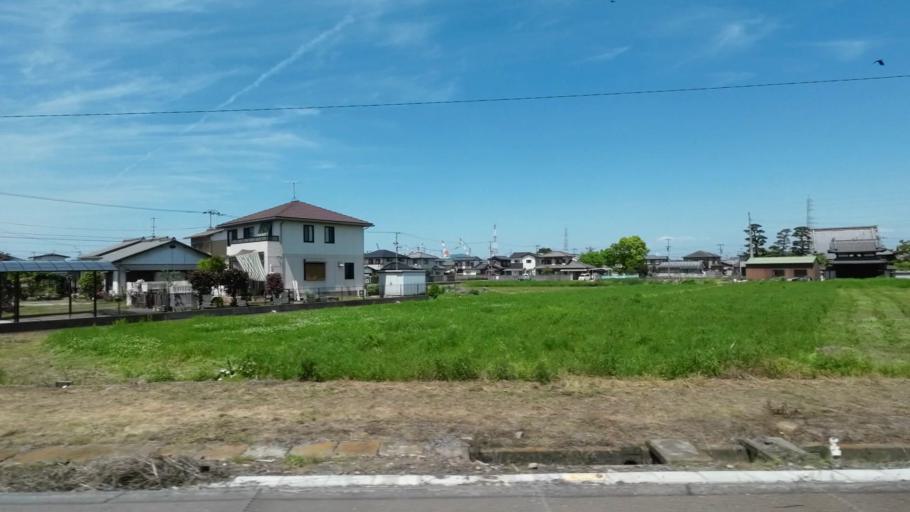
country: JP
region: Kagawa
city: Tadotsu
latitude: 34.2784
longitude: 133.7611
